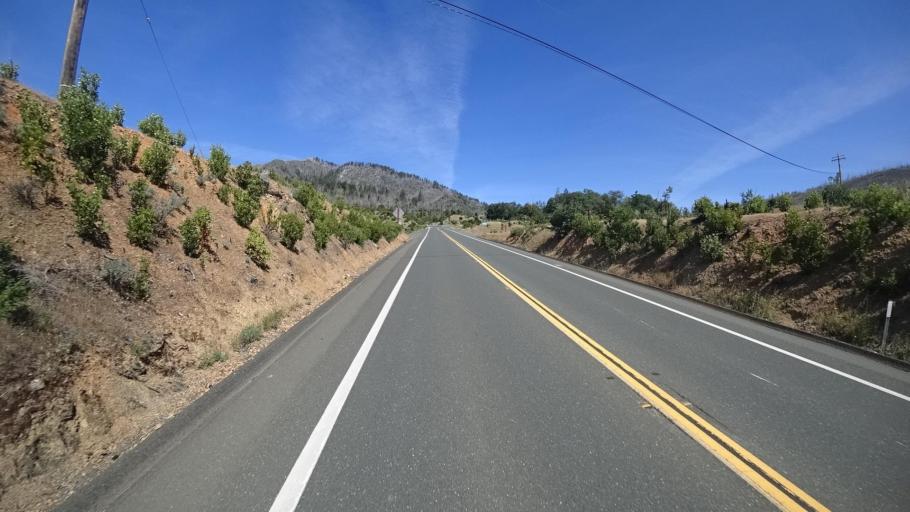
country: US
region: California
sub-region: Lake County
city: Cobb
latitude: 38.7927
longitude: -122.7020
